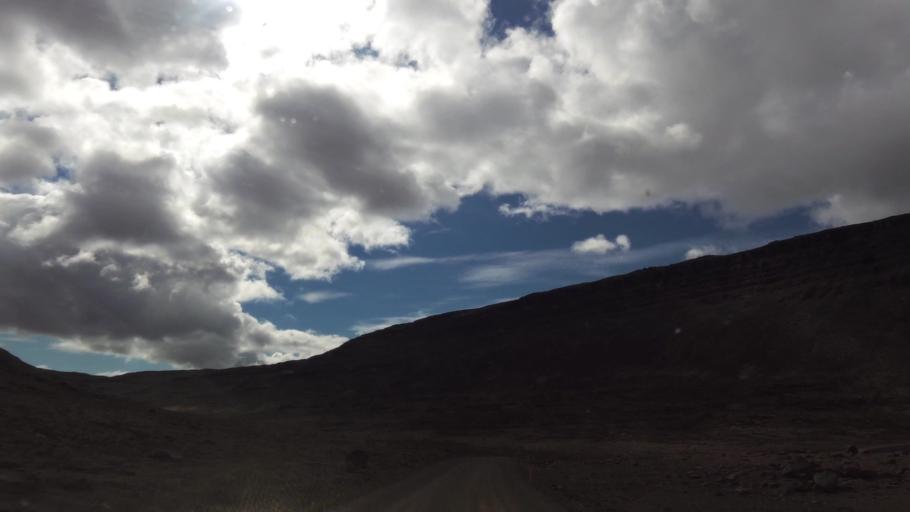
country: IS
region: West
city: Olafsvik
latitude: 65.5757
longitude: -24.0794
